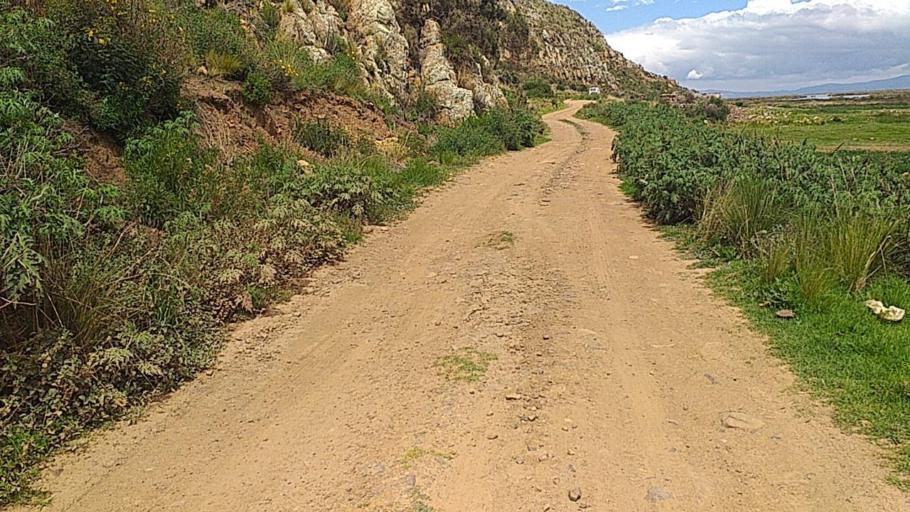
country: BO
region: La Paz
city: Batallas
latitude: -16.3232
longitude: -68.6485
